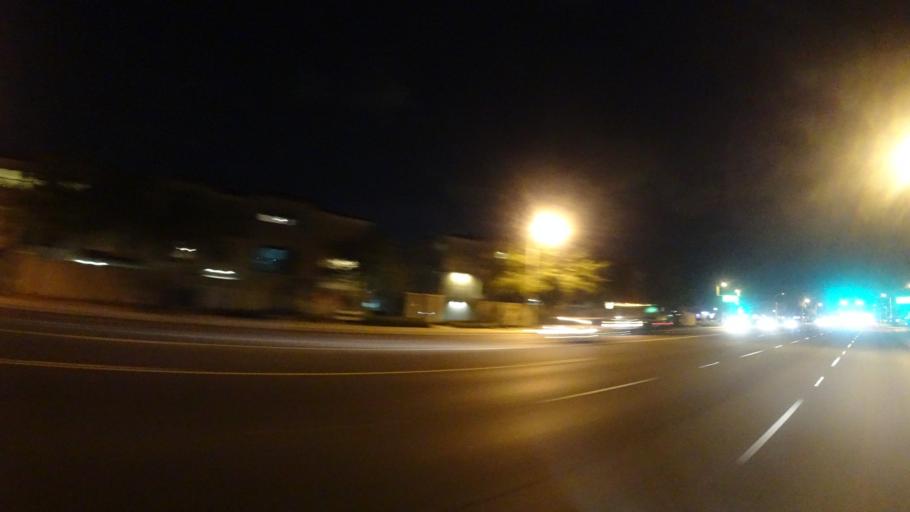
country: US
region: Arizona
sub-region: Maricopa County
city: Guadalupe
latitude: 33.3783
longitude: -111.9342
